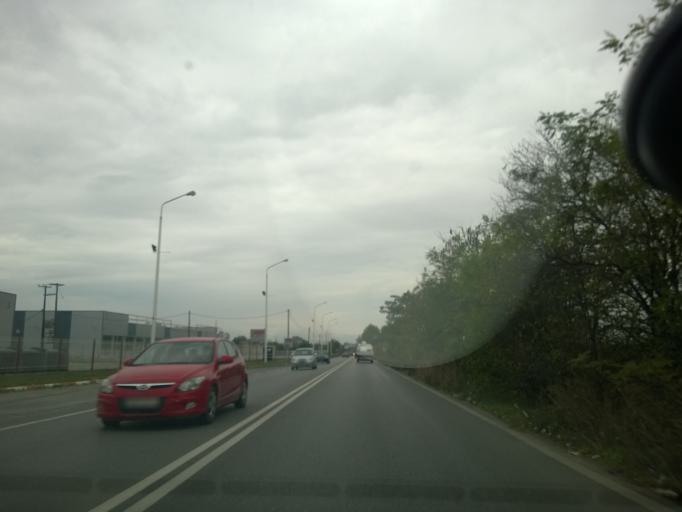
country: GR
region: Central Macedonia
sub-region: Nomos Pellis
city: Melissi
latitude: 40.7802
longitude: 22.3737
